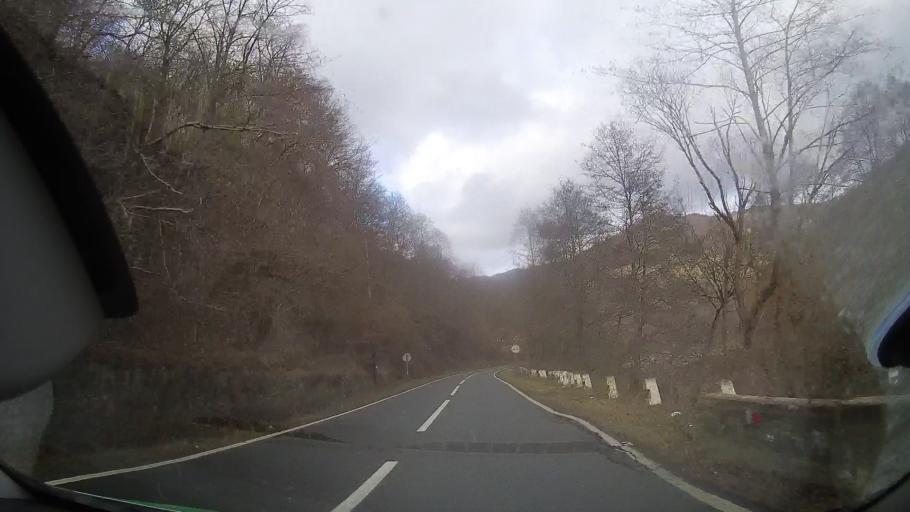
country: RO
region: Cluj
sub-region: Comuna Iara
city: Iara
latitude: 46.4939
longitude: 23.5295
